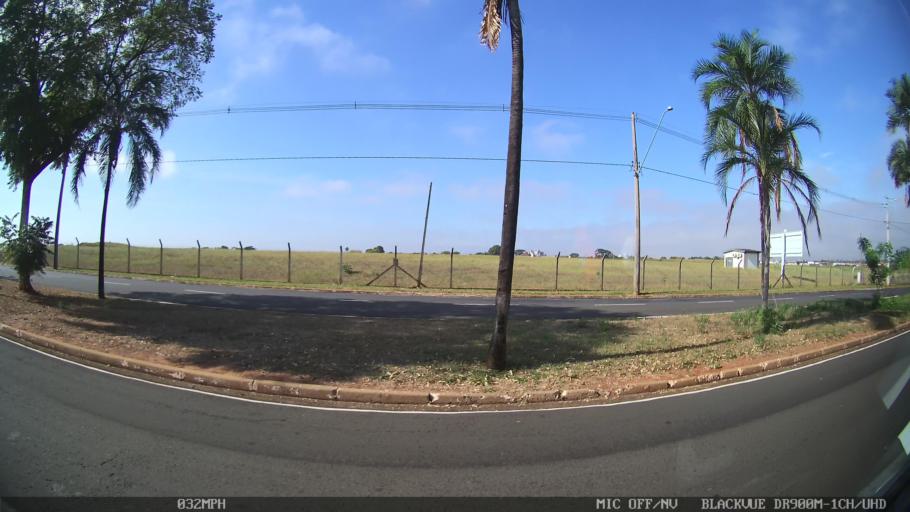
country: BR
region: Sao Paulo
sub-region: Sao Jose Do Rio Preto
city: Sao Jose do Rio Preto
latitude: -20.8196
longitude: -49.4148
